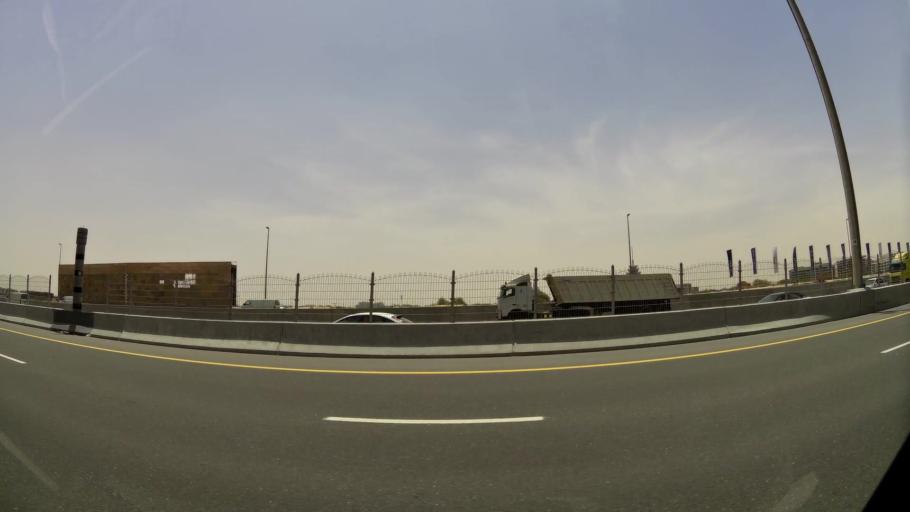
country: AE
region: Ash Shariqah
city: Sharjah
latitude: 25.1301
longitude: 55.3765
